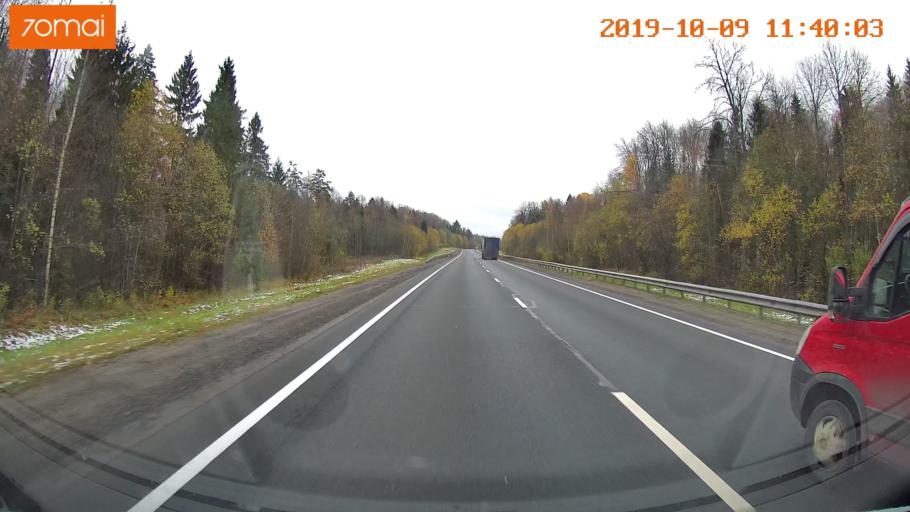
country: RU
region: Vologda
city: Gryazovets
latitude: 58.9475
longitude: 40.1728
